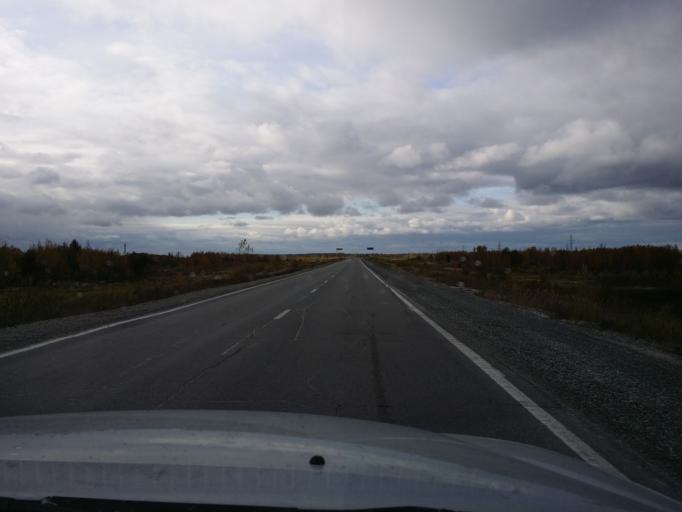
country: RU
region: Khanty-Mansiyskiy Avtonomnyy Okrug
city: Langepas
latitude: 61.1863
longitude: 75.4597
